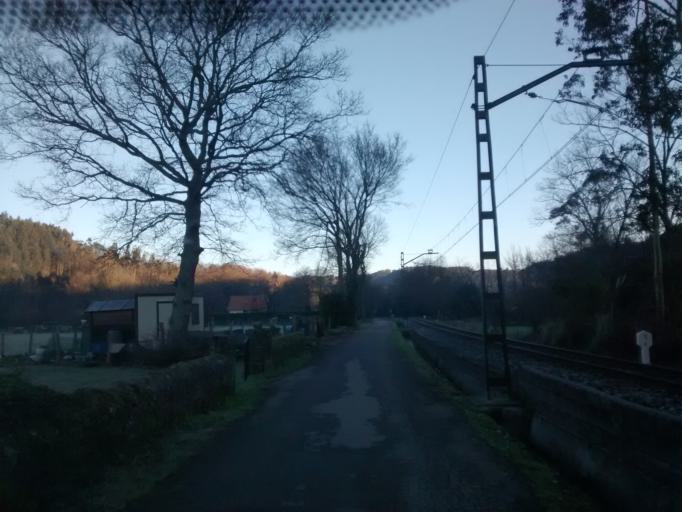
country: ES
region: Cantabria
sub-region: Provincia de Cantabria
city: Lierganes
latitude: 43.3611
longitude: -3.7138
